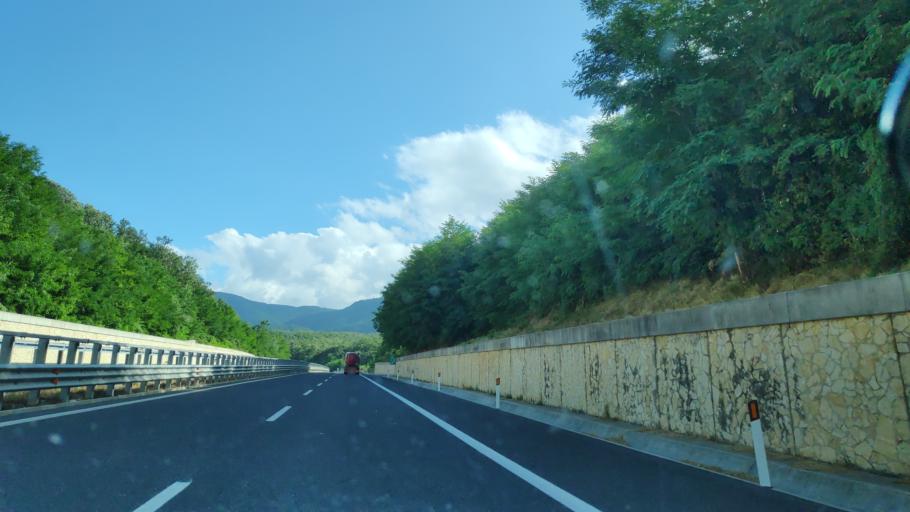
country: IT
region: Campania
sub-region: Provincia di Salerno
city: Casalbuono
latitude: 40.2439
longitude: 15.6596
